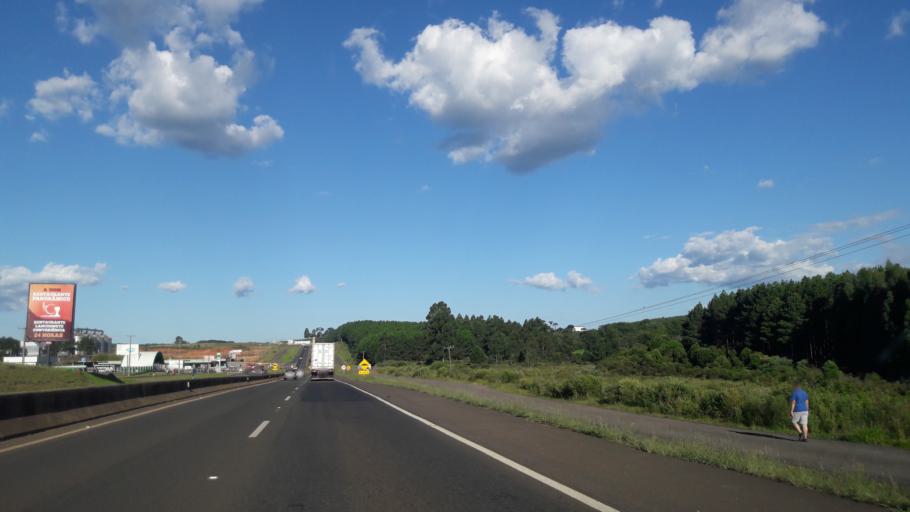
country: BR
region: Parana
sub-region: Guarapuava
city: Guarapuava
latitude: -25.3458
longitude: -51.4455
